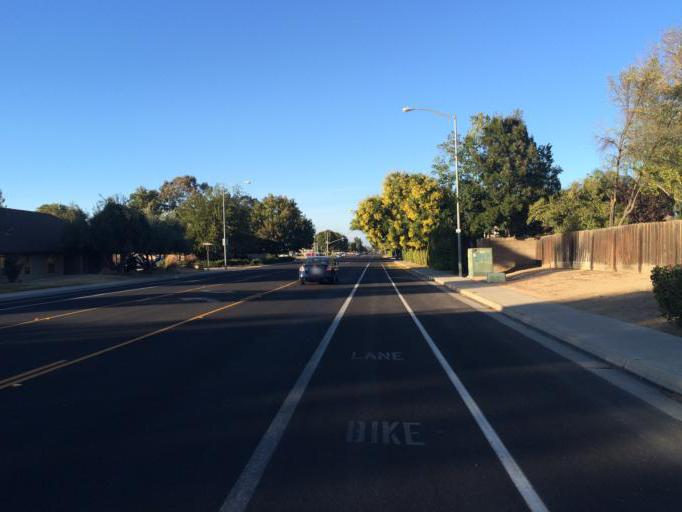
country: US
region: California
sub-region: Fresno County
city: Tarpey Village
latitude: 36.8063
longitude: -119.6730
